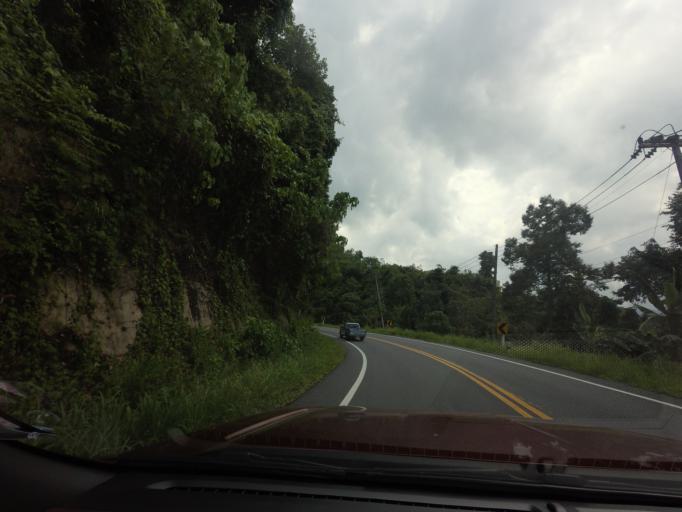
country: TH
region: Yala
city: Than To
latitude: 6.0371
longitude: 101.2033
